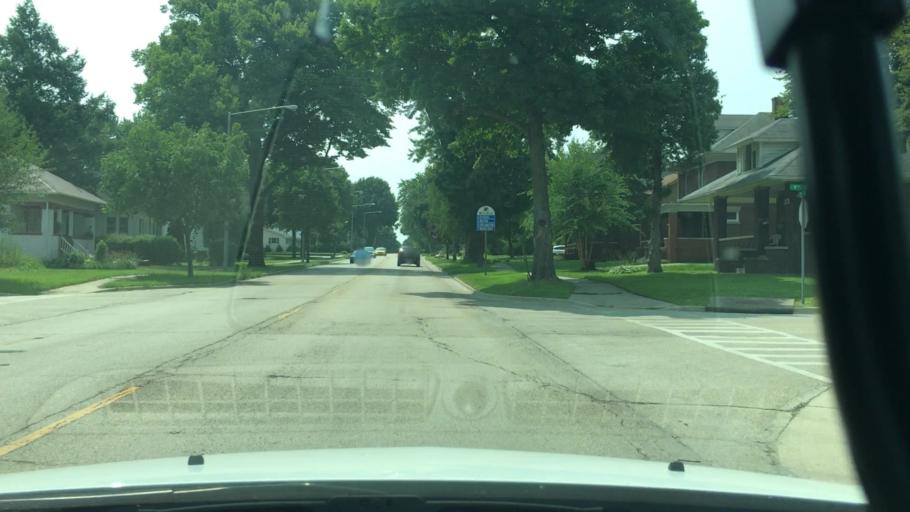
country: US
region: Illinois
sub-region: Ogle County
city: Rochelle
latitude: 41.9283
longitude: -89.0689
